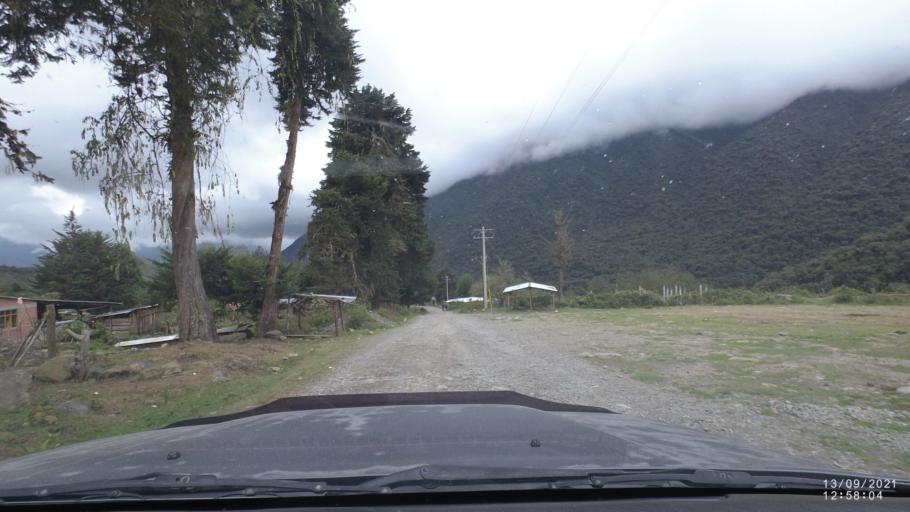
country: BO
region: Cochabamba
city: Colomi
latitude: -17.2386
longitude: -65.8173
